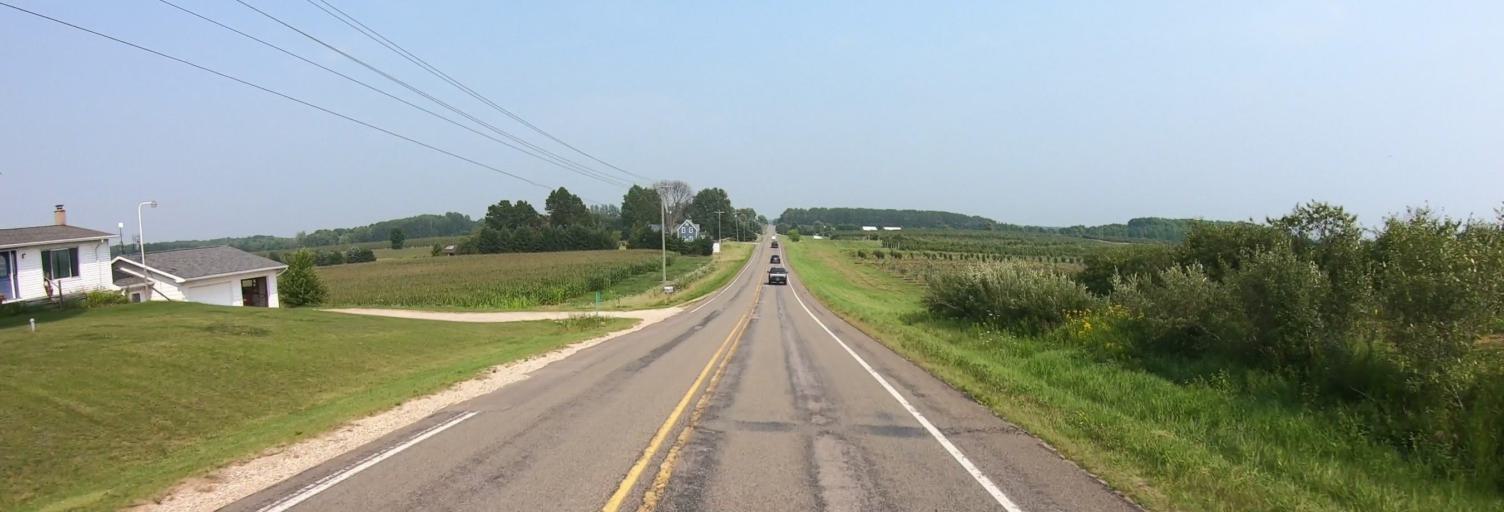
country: US
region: Michigan
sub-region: Charlevoix County
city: Charlevoix
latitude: 45.1860
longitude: -85.3395
